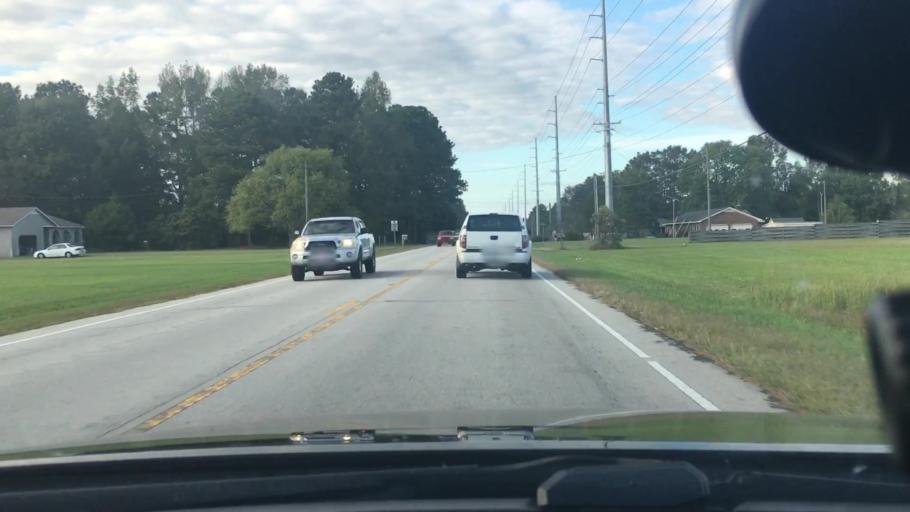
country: US
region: North Carolina
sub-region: Pitt County
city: Windsor
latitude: 35.5394
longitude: -77.3220
